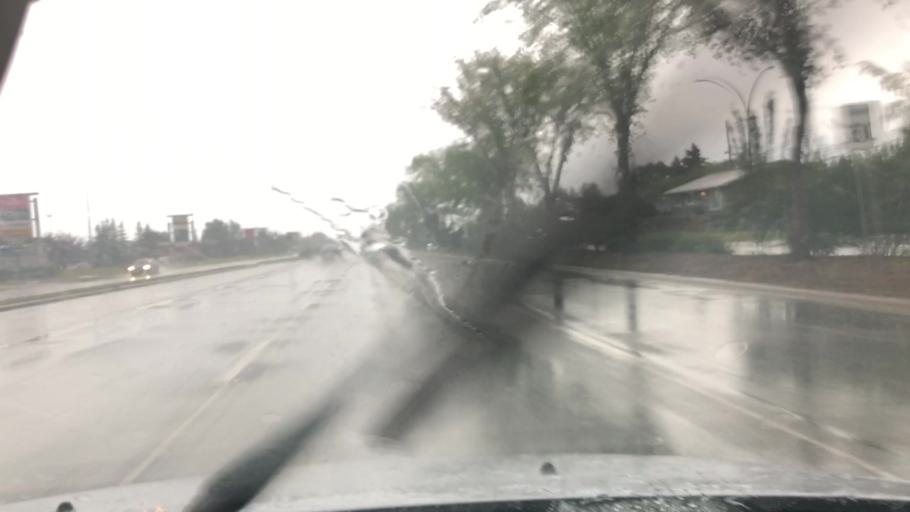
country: CA
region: Alberta
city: St. Albert
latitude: 53.5993
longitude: -113.5609
